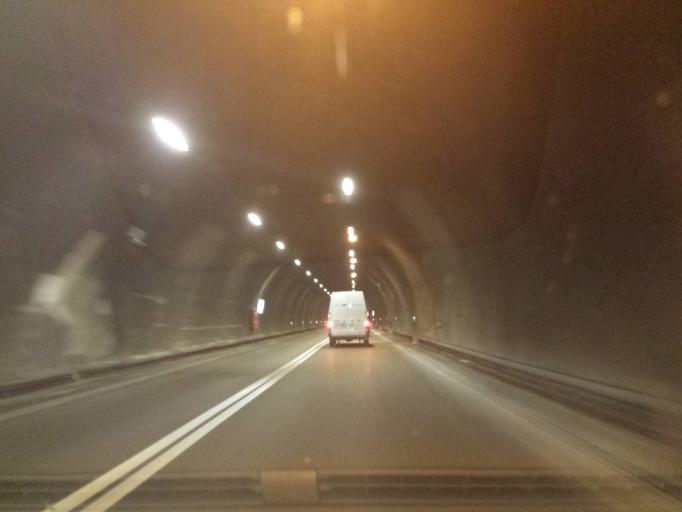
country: IT
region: Lombardy
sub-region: Provincia di Brescia
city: Gavardo-Sopraponte
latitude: 45.5862
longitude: 10.4543
